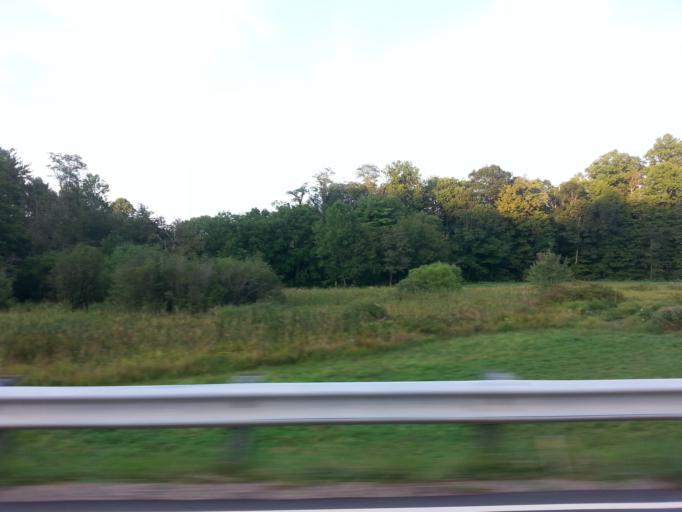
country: US
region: Tennessee
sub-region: Johnson County
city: Mountain City
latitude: 36.5474
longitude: -81.8964
